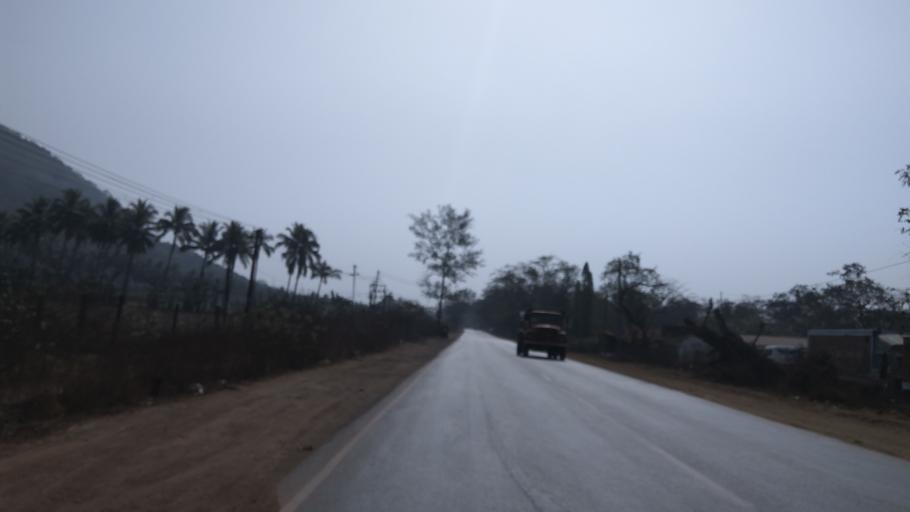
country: IN
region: Goa
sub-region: North Goa
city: Palle
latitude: 15.4035
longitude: 74.0959
